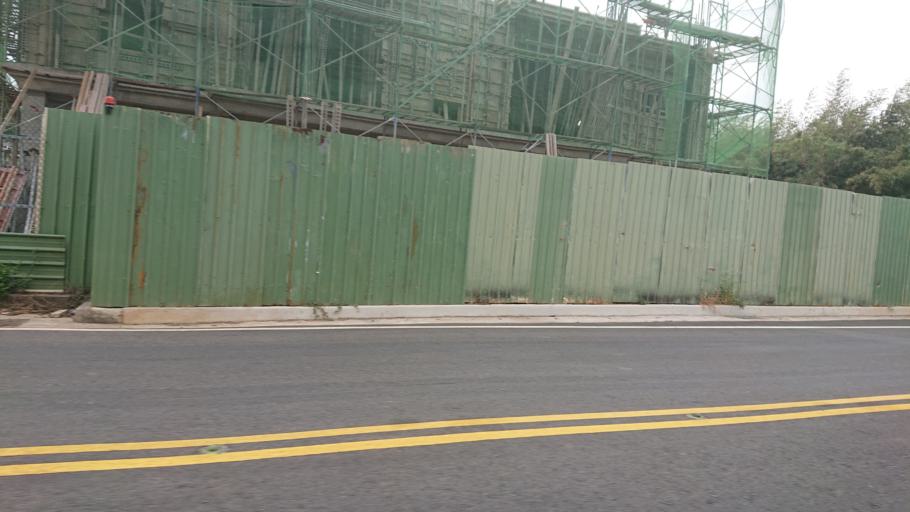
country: TW
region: Fukien
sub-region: Kinmen
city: Jincheng
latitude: 24.4166
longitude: 118.3142
